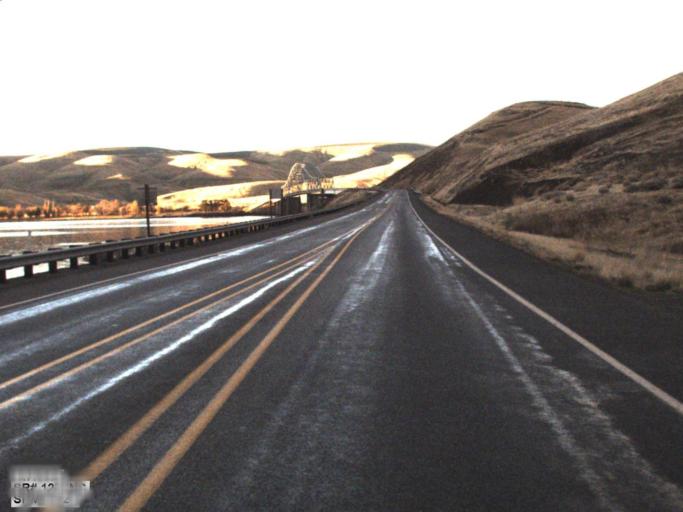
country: US
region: Washington
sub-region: Garfield County
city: Pomeroy
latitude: 46.6188
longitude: -117.7935
